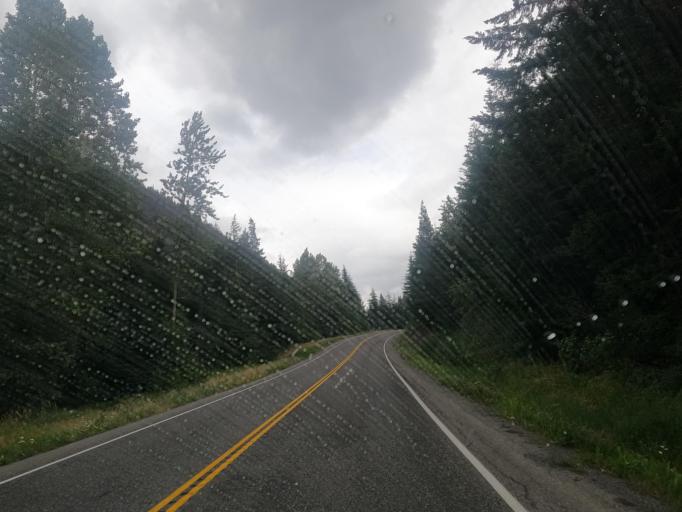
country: CA
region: British Columbia
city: Lillooet
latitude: 50.4898
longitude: -122.2016
